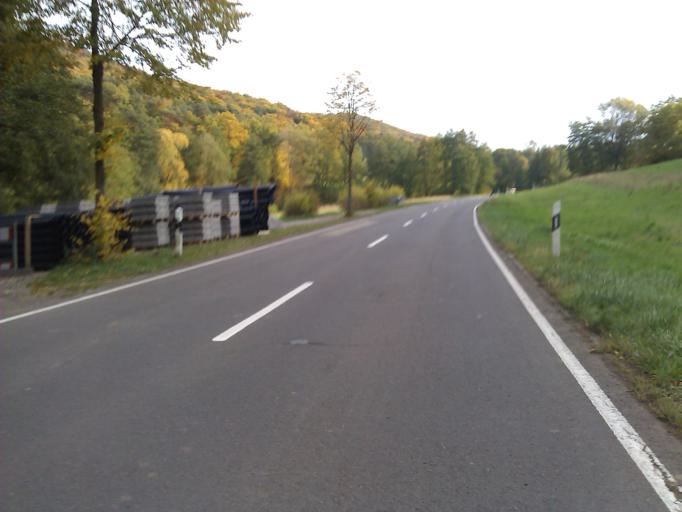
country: DE
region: Rheinland-Pfalz
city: Hefersweiler
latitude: 49.5943
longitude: 7.6907
